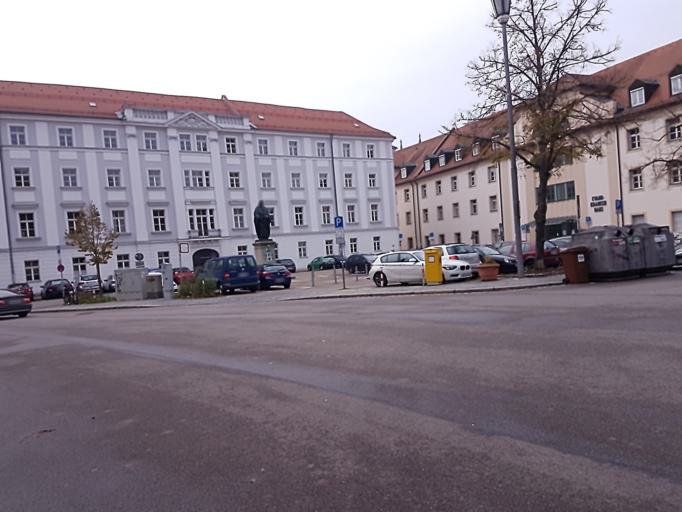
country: DE
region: Bavaria
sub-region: Upper Palatinate
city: Lappersdorf
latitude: 49.0163
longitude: 12.0927
